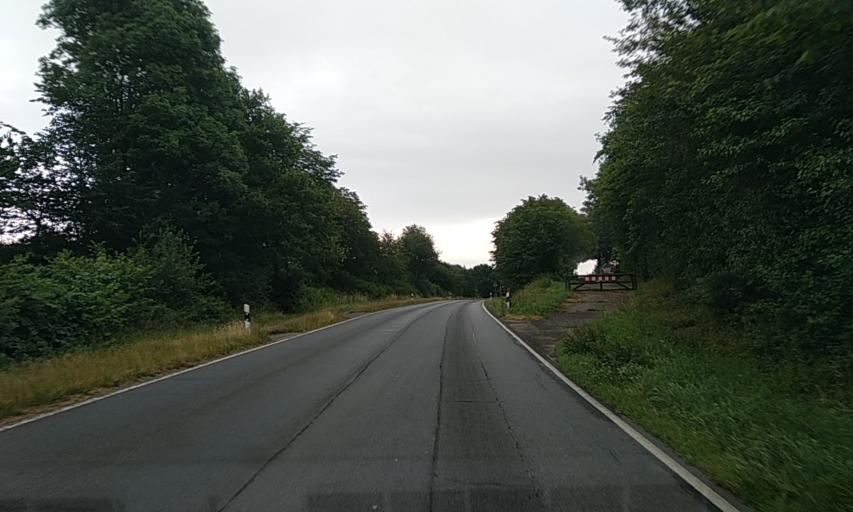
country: DE
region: Schleswig-Holstein
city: Boel
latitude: 54.6460
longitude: 9.7282
